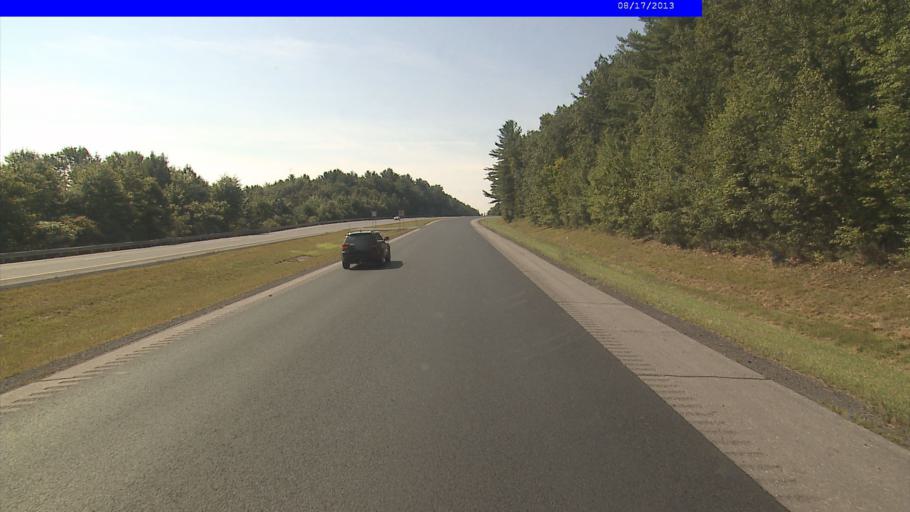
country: US
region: Vermont
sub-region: Windham County
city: Bellows Falls
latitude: 43.0981
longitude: -72.4542
